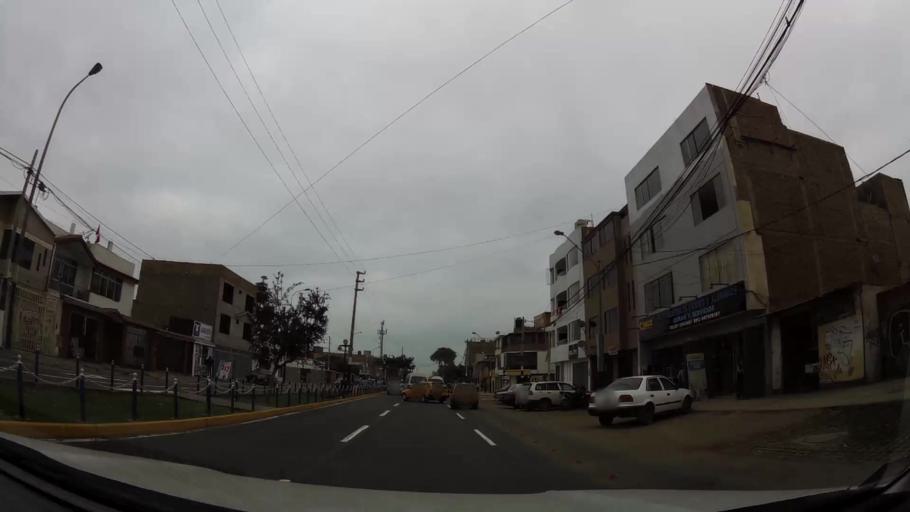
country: PE
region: Lima
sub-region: Lima
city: Surco
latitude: -12.2003
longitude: -77.0136
